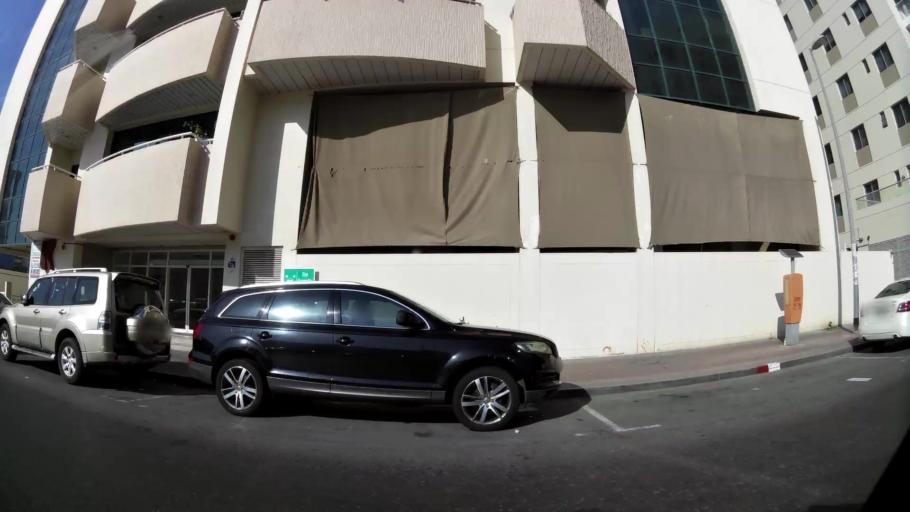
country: AE
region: Ash Shariqah
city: Sharjah
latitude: 25.2558
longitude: 55.2920
